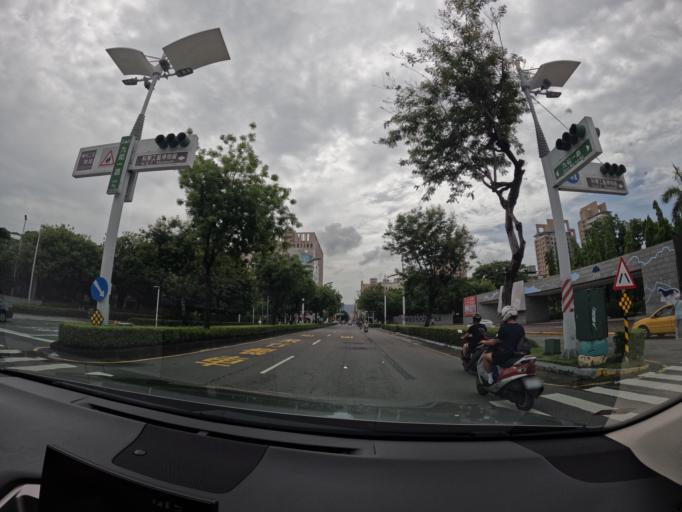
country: TW
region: Kaohsiung
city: Kaohsiung
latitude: 22.6398
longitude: 120.3224
